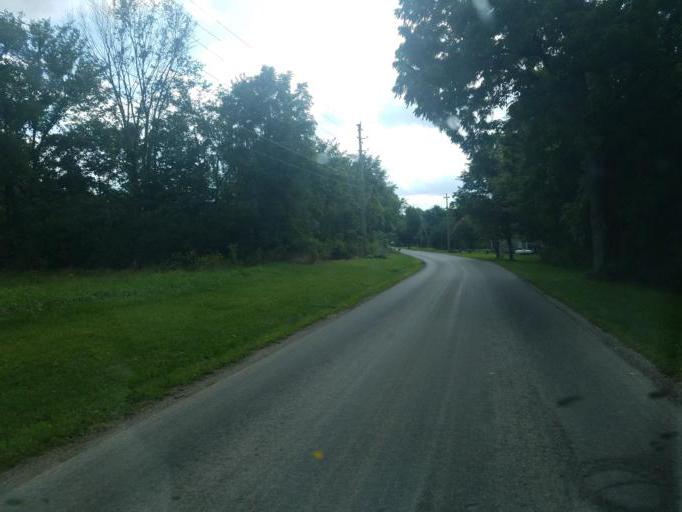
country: US
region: Ohio
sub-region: Huron County
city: Greenwich
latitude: 40.9353
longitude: -82.5298
